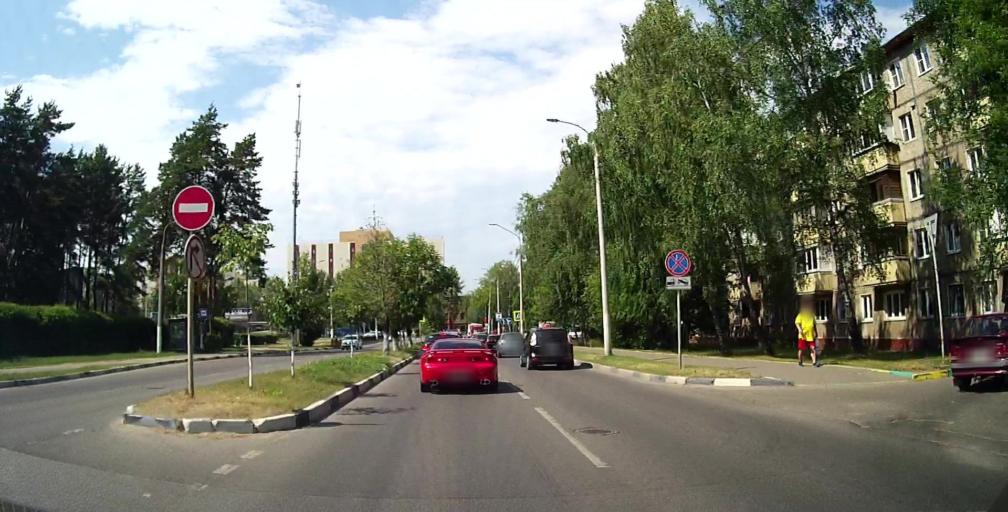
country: RU
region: Moskovskaya
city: Dubrovitsy
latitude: 55.4208
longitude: 37.5178
